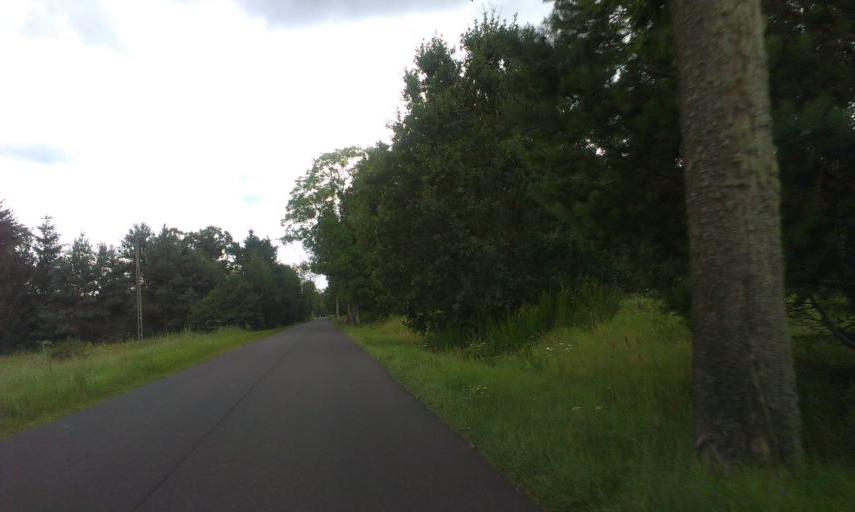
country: PL
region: West Pomeranian Voivodeship
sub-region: Powiat bialogardzki
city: Tychowo
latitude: 53.8616
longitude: 16.1651
